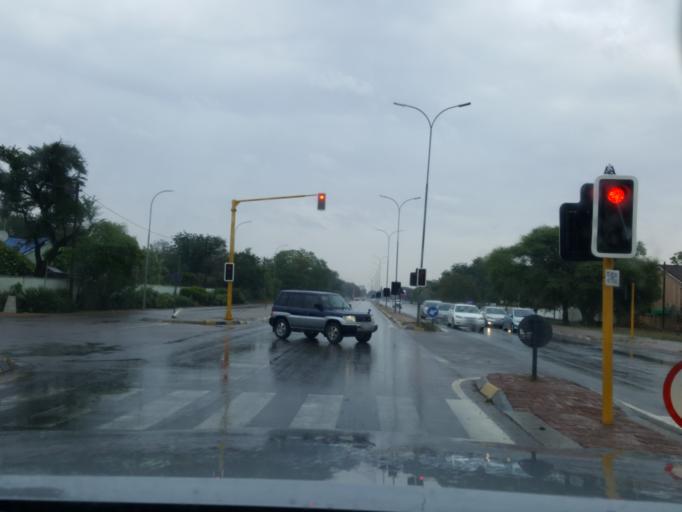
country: BW
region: South East
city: Gaborone
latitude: -24.6437
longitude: 25.9254
